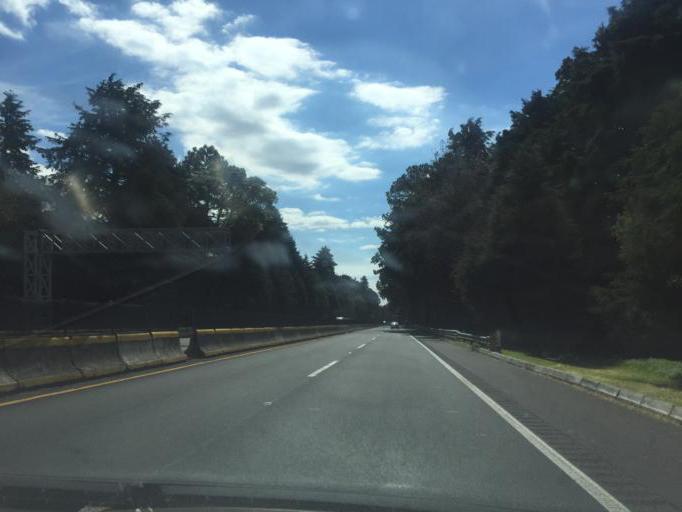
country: MX
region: Morelos
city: Tres Marias
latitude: 19.0450
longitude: -99.2352
